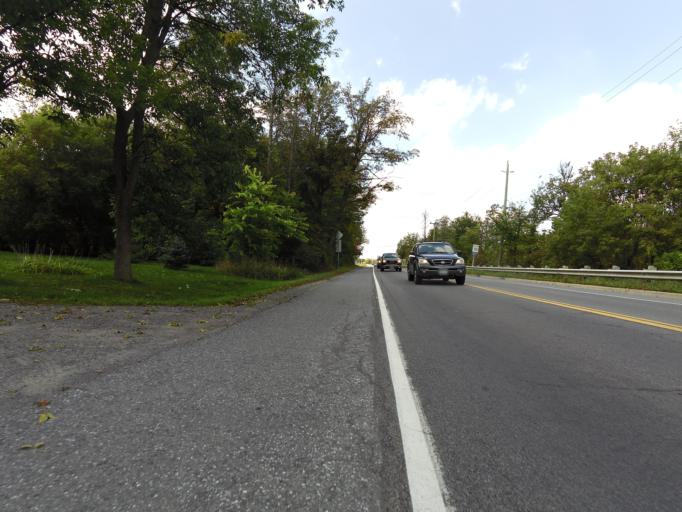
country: CA
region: Ontario
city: Bells Corners
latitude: 45.2316
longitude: -75.6944
